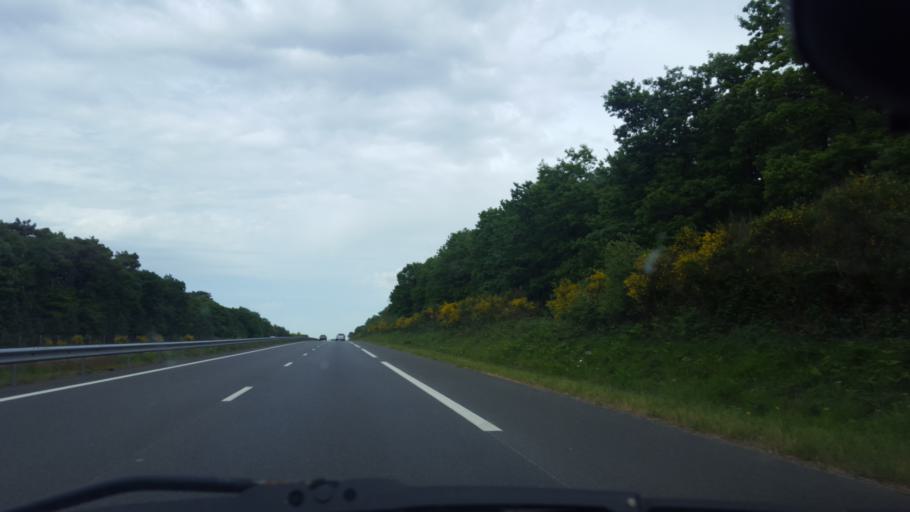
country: FR
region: Pays de la Loire
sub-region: Departement de la Loire-Atlantique
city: Saint-Lumine-de-Coutais
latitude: 47.0088
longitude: -1.7125
